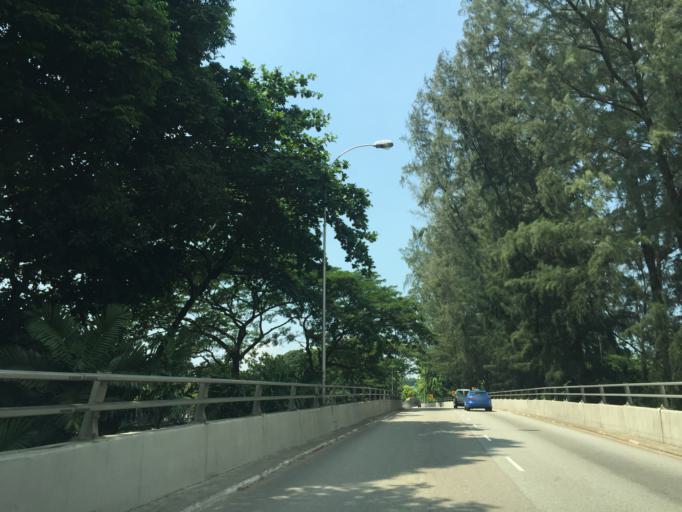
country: SG
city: Singapore
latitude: 1.3139
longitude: 103.8385
